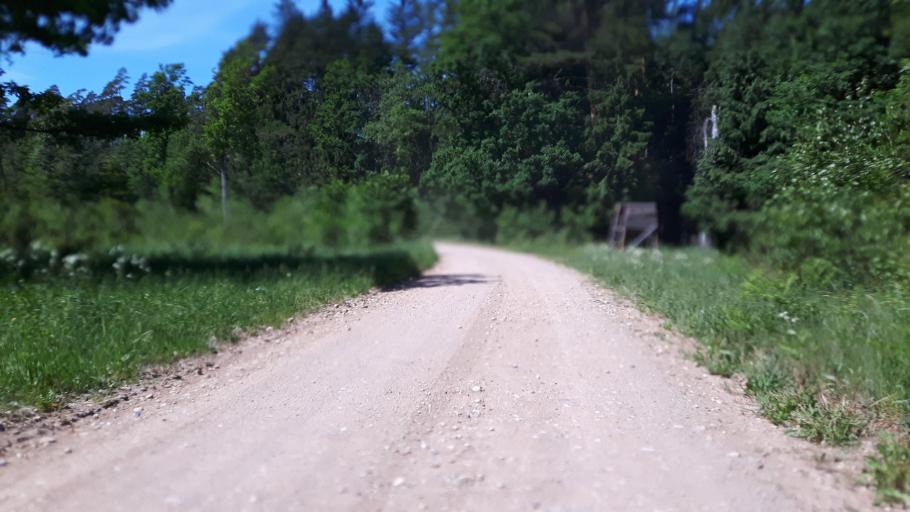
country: LV
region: Kandava
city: Kandava
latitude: 57.0427
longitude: 22.8445
